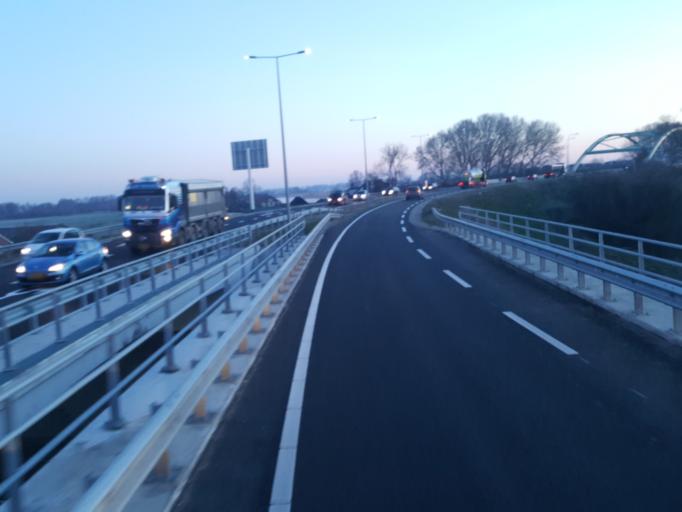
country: NL
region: Overijssel
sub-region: Gemeente Zwartewaterland
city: Hasselt
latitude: 52.5896
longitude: 6.0822
